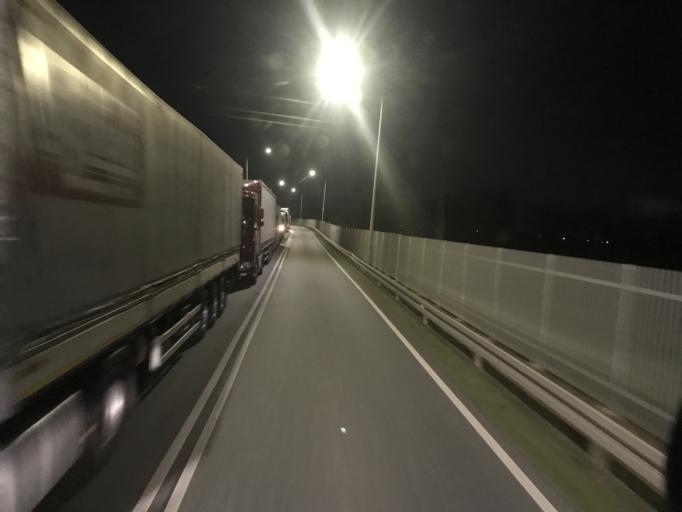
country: PL
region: Lublin Voivodeship
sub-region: Powiat bialski
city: Terespol
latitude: 52.0809
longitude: 23.5293
